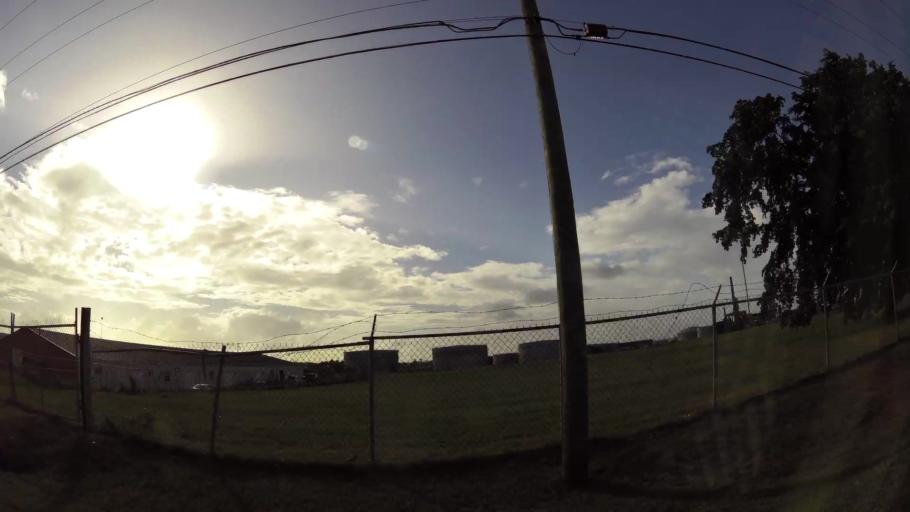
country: AG
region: Saint John
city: Saint John's
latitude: 17.1377
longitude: -61.8361
